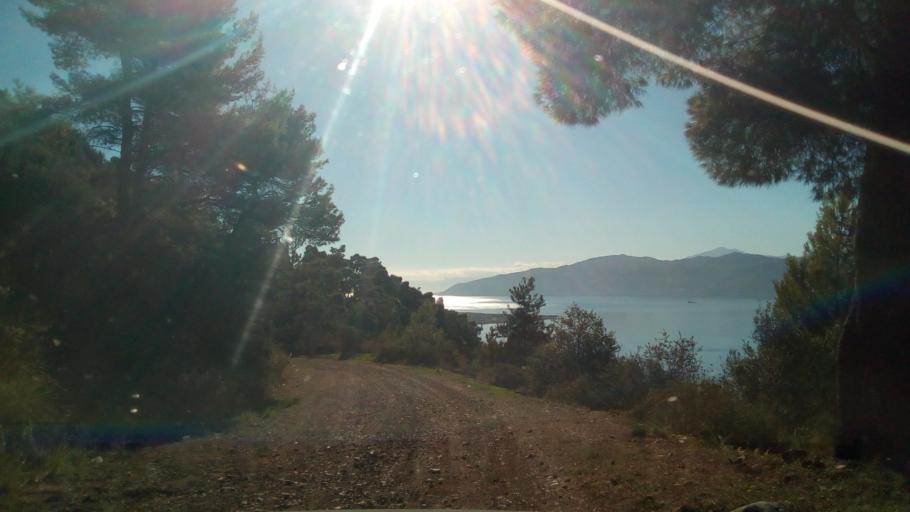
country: GR
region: West Greece
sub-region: Nomos Aitolias kai Akarnanias
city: Nafpaktos
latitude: 38.3965
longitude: 21.8218
